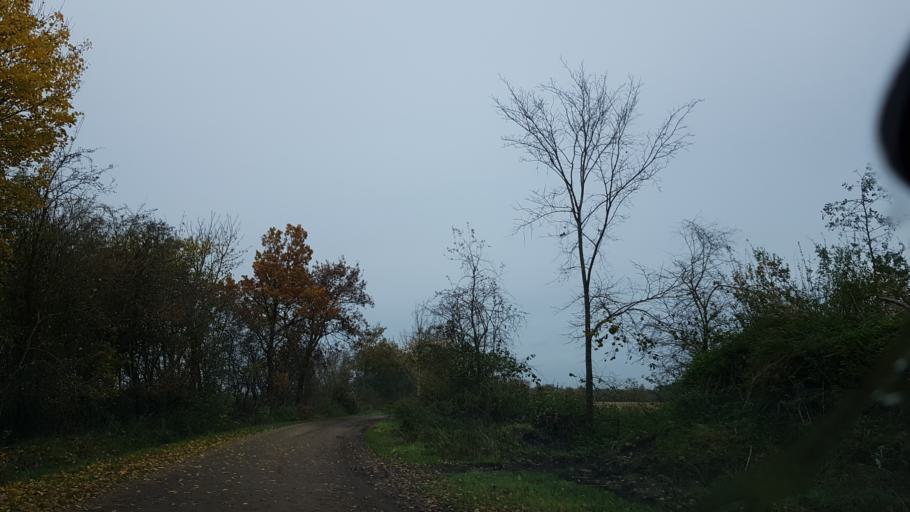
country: DK
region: South Denmark
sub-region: Tonder Kommune
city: Sherrebek
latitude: 55.2185
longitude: 8.8661
